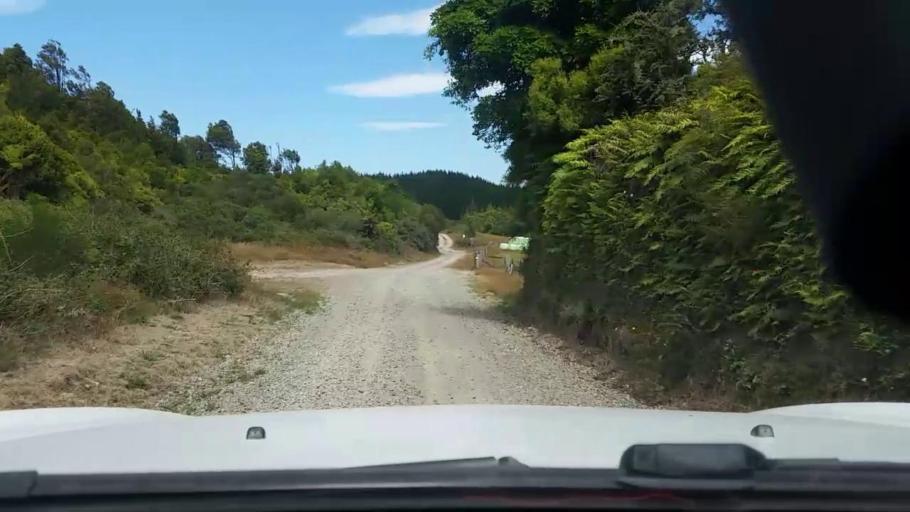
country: NZ
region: Bay of Plenty
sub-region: Rotorua District
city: Rotorua
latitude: -37.9890
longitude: 176.1632
